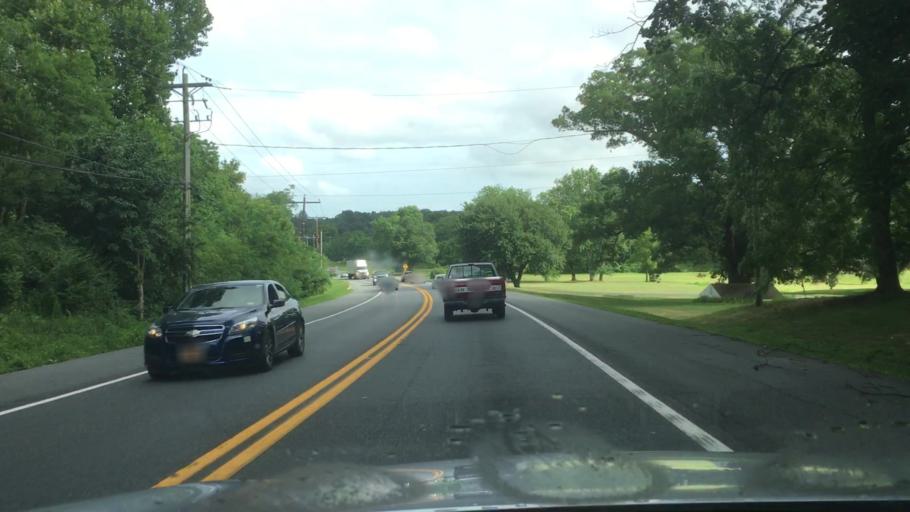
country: US
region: Delaware
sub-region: New Castle County
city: North Star
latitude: 39.7782
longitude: -75.7192
